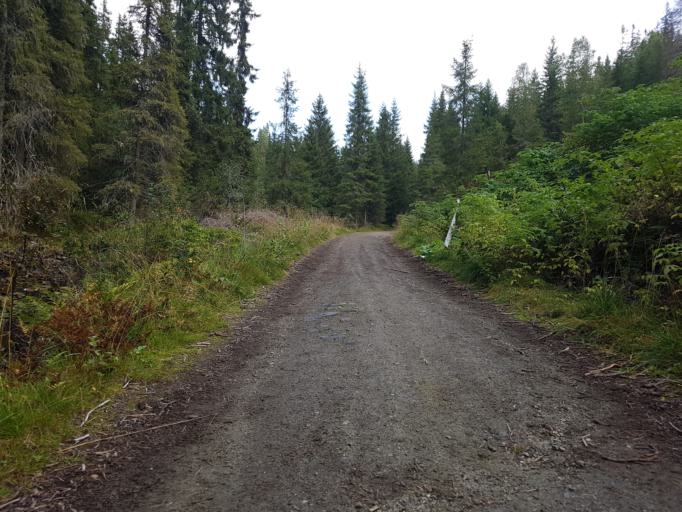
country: NO
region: Sor-Trondelag
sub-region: Melhus
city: Melhus
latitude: 63.4307
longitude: 10.2080
